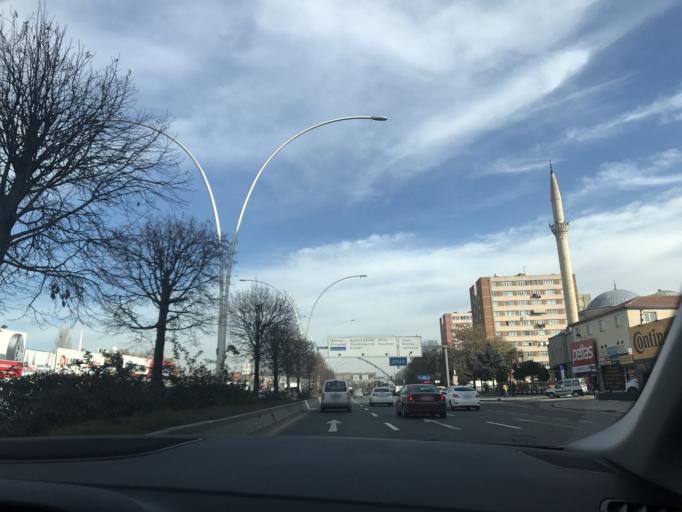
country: TR
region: Ankara
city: Ankara
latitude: 39.9556
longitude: 32.8441
